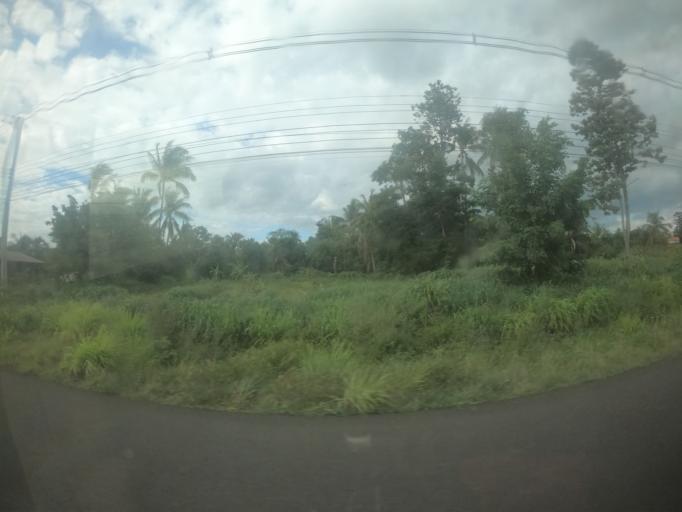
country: TH
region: Surin
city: Prasat
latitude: 14.5640
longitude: 103.4952
